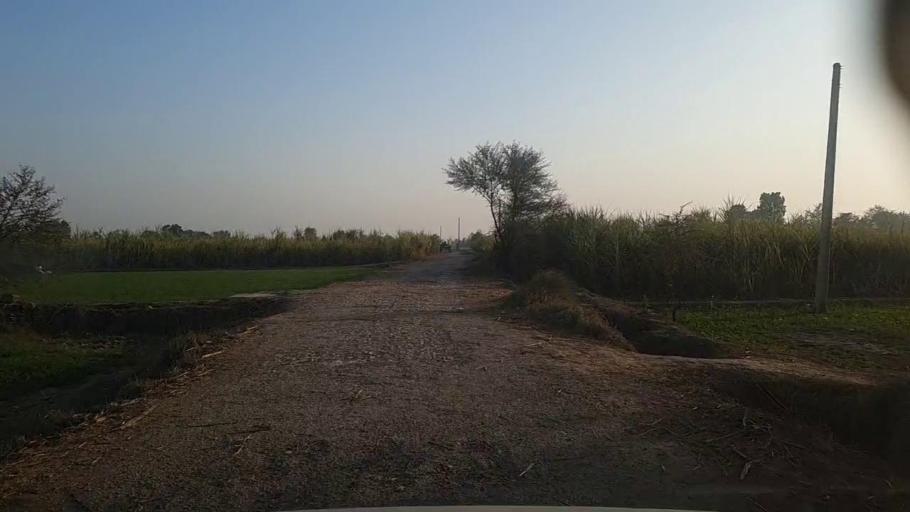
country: PK
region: Sindh
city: Khairpur
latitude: 28.0595
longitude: 69.7576
